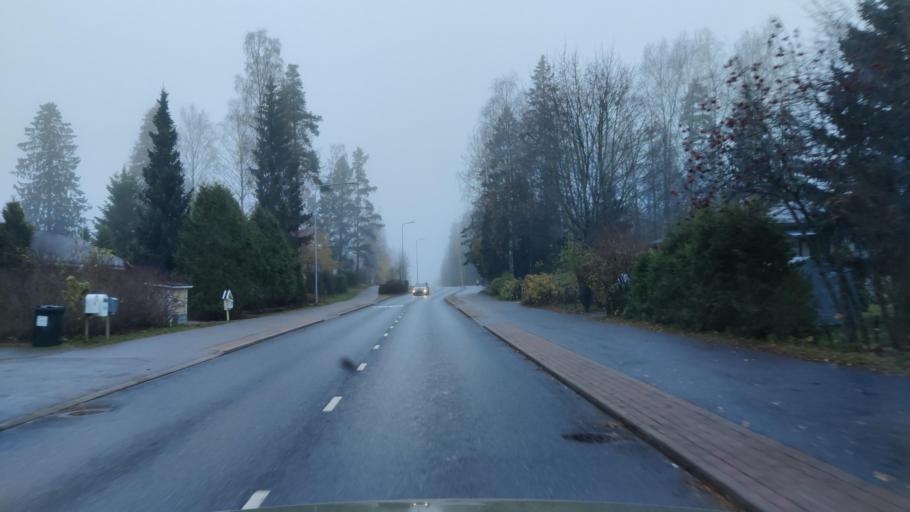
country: FI
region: Uusimaa
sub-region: Helsinki
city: Kerava
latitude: 60.3594
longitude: 25.0955
